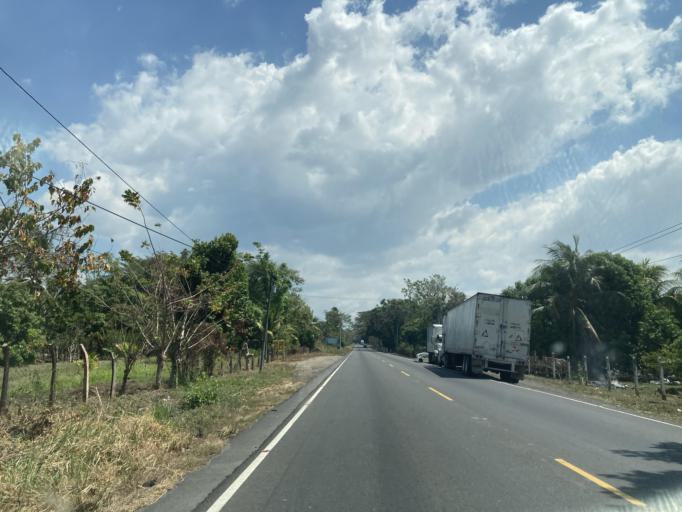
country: GT
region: Santa Rosa
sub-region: Municipio de Taxisco
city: Taxisco
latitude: 14.0931
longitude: -90.5554
